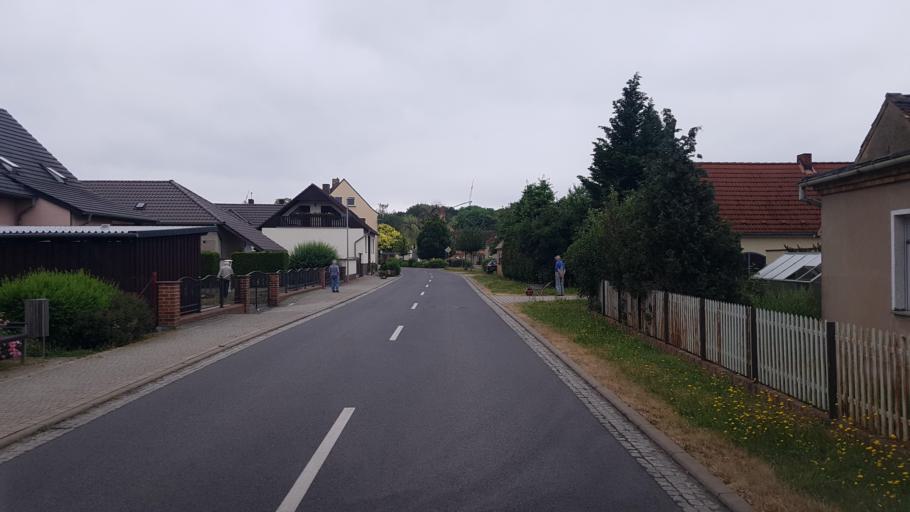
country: DE
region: Brandenburg
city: Schwarzbach
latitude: 51.4733
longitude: 13.9424
